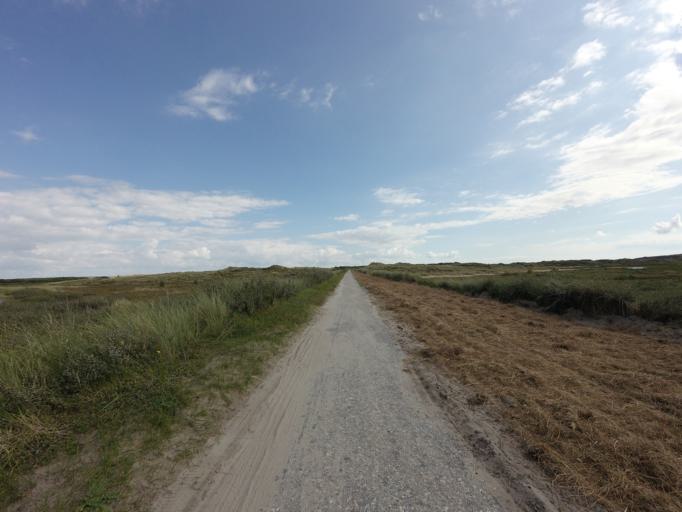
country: NL
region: Friesland
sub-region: Gemeente Terschelling
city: West-Terschelling
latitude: 53.3973
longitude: 5.2615
